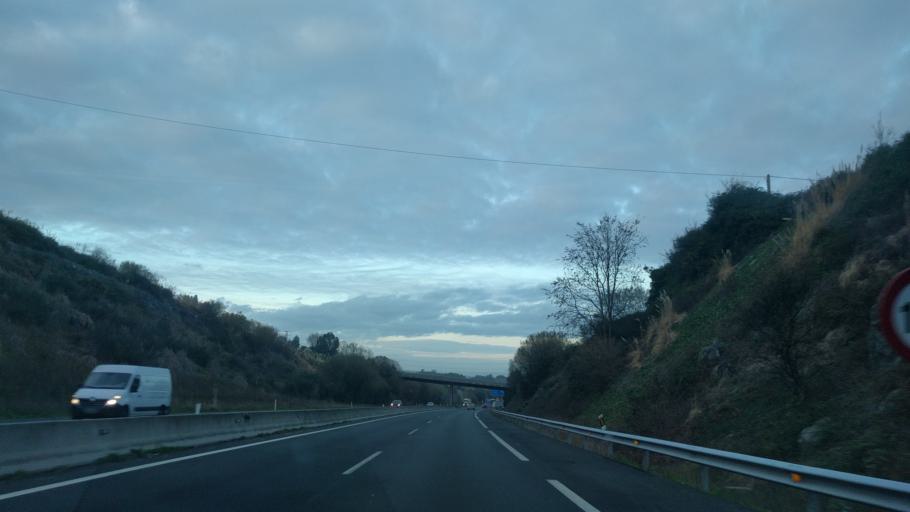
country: ES
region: Cantabria
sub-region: Provincia de Cantabria
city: Castro-Urdiales
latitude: 43.3826
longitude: -3.2319
